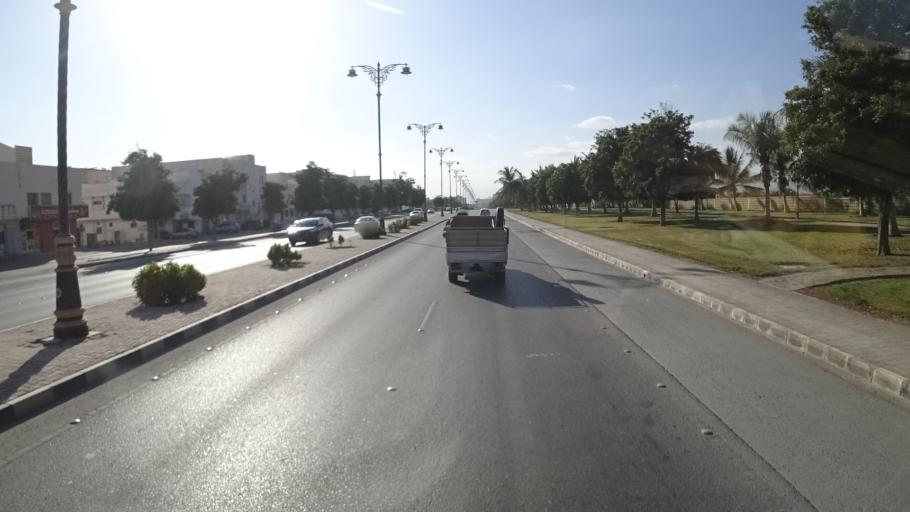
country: OM
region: Zufar
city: Salalah
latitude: 17.0048
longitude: 54.0509
